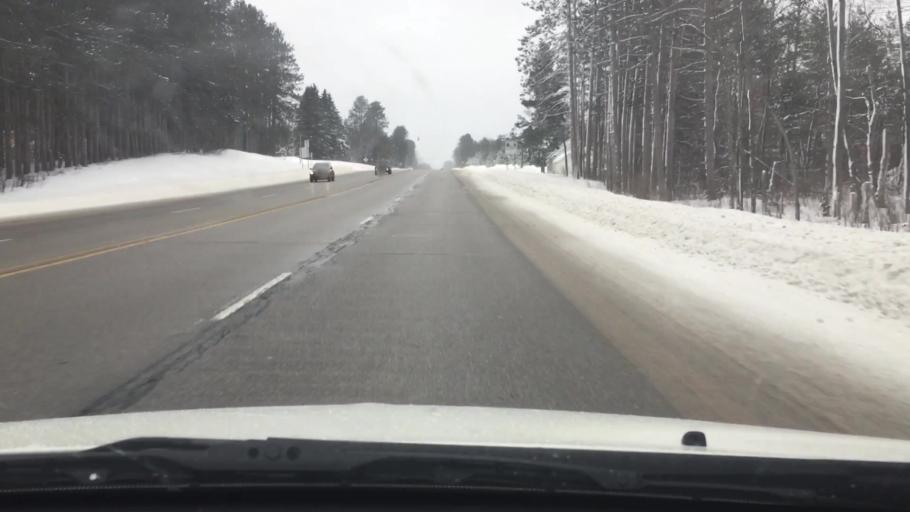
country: US
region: Michigan
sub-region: Otsego County
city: Gaylord
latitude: 45.0414
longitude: -84.7758
